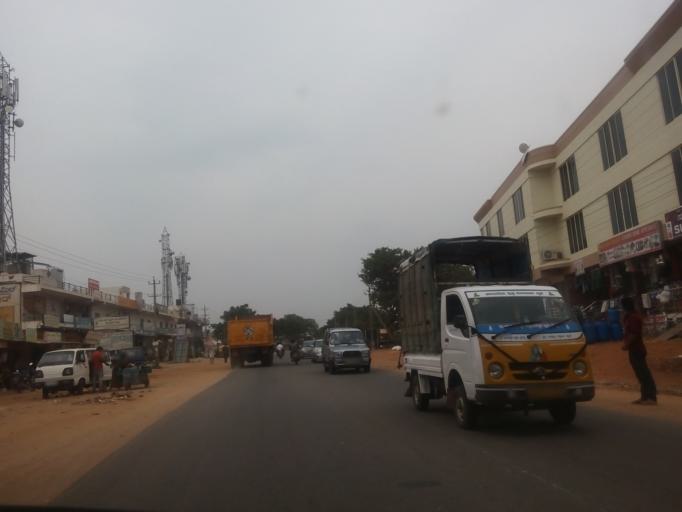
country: IN
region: Karnataka
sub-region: Bangalore Rural
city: Nelamangala
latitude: 12.9897
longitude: 77.4506
